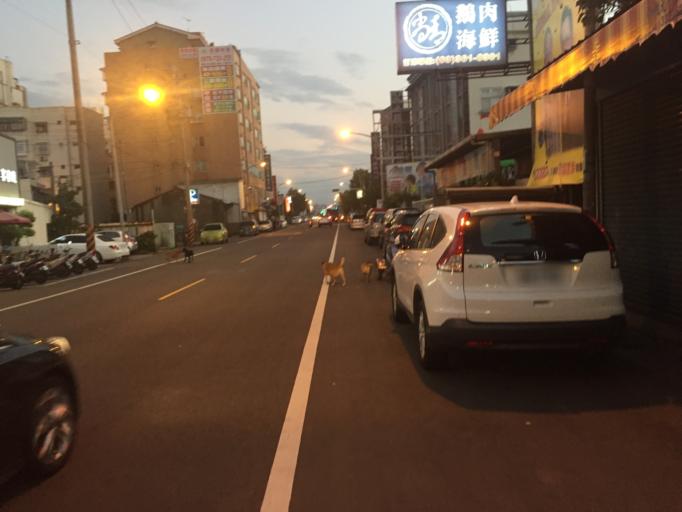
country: TW
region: Taiwan
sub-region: Taoyuan
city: Taoyuan
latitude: 24.9798
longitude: 121.3146
